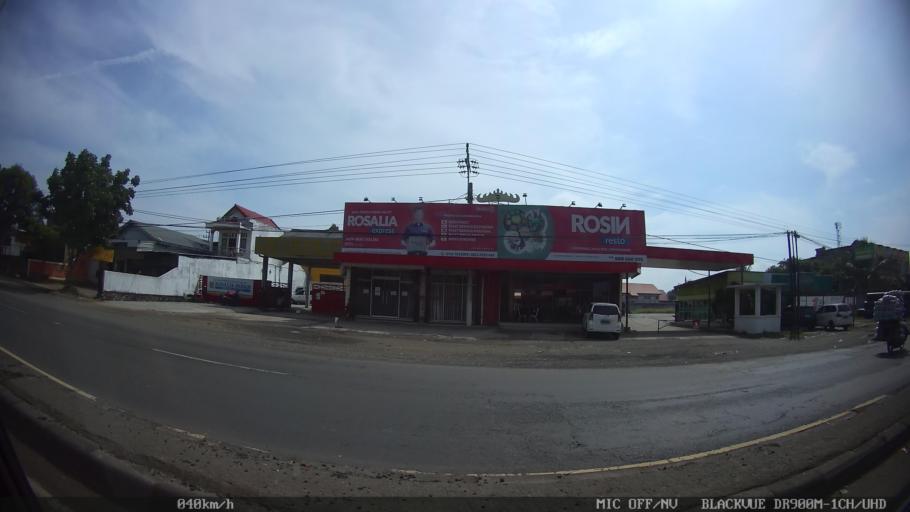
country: ID
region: Lampung
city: Kedaton
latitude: -5.3700
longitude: 105.2722
